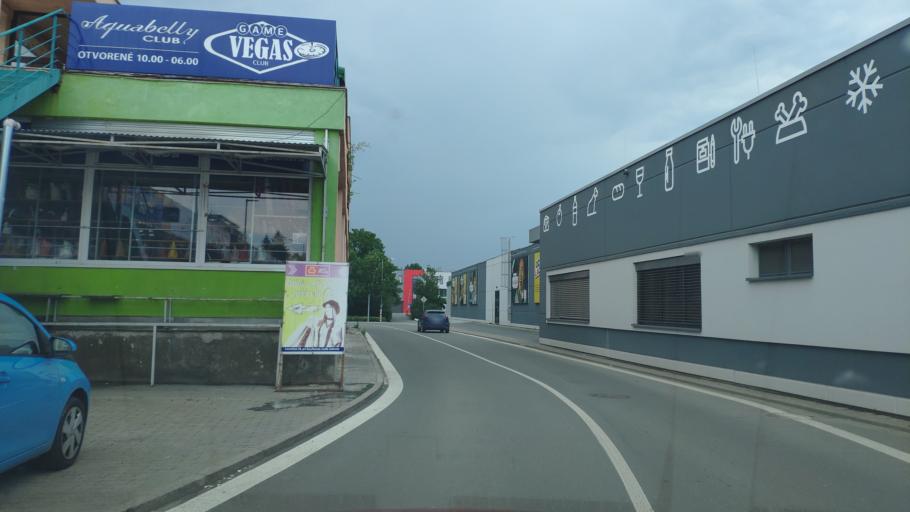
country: SK
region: Presovsky
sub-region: Okres Presov
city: Presov
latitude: 49.0012
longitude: 21.2281
